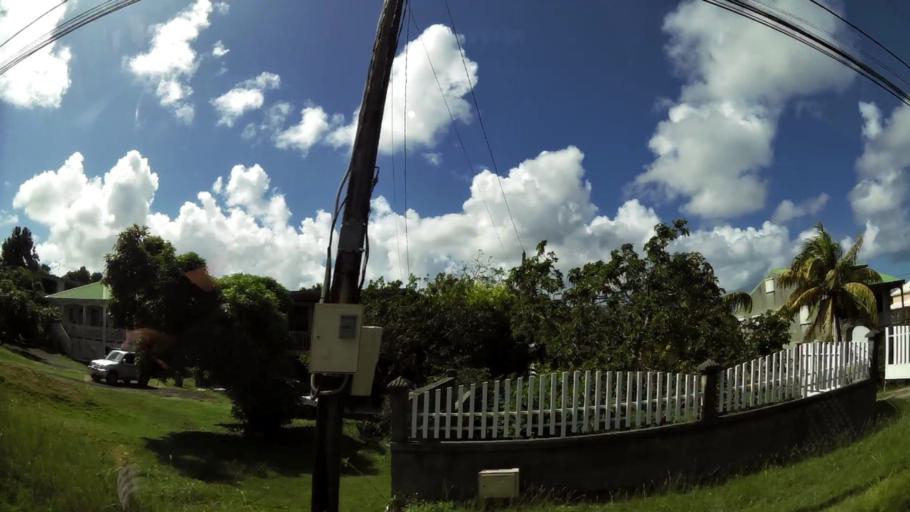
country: GP
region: Guadeloupe
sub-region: Guadeloupe
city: Anse-Bertrand
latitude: 16.4583
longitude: -61.4812
